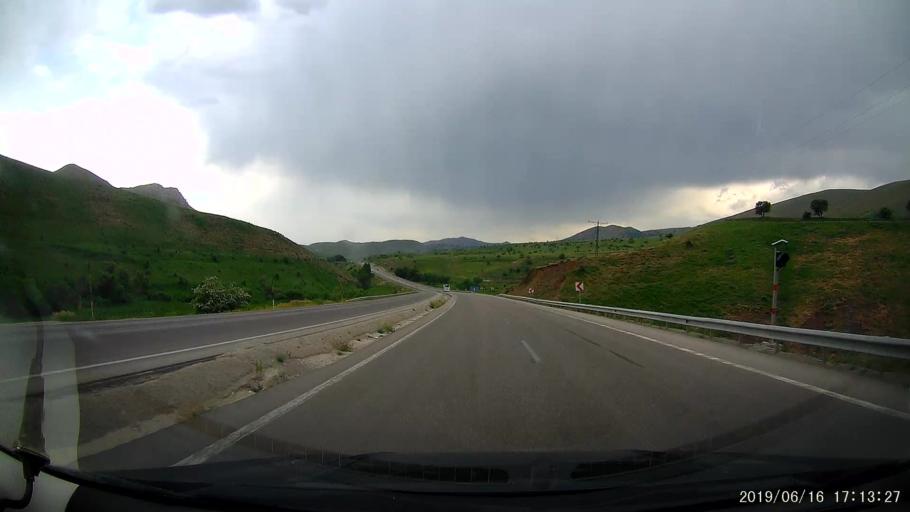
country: TR
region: Erzurum
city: Askale
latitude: 39.8593
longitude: 40.5982
